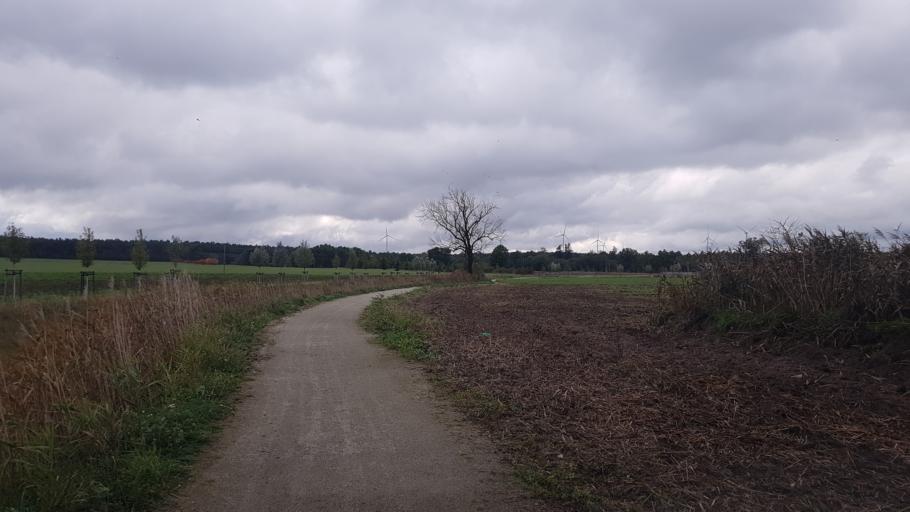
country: DE
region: Brandenburg
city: Altdobern
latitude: 51.6467
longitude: 14.0303
